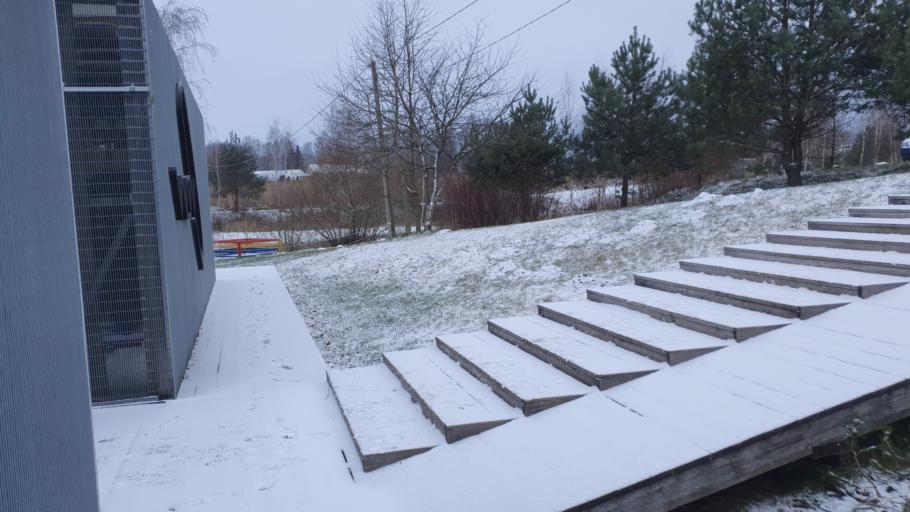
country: LT
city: Skaidiskes
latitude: 54.6381
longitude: 25.3761
